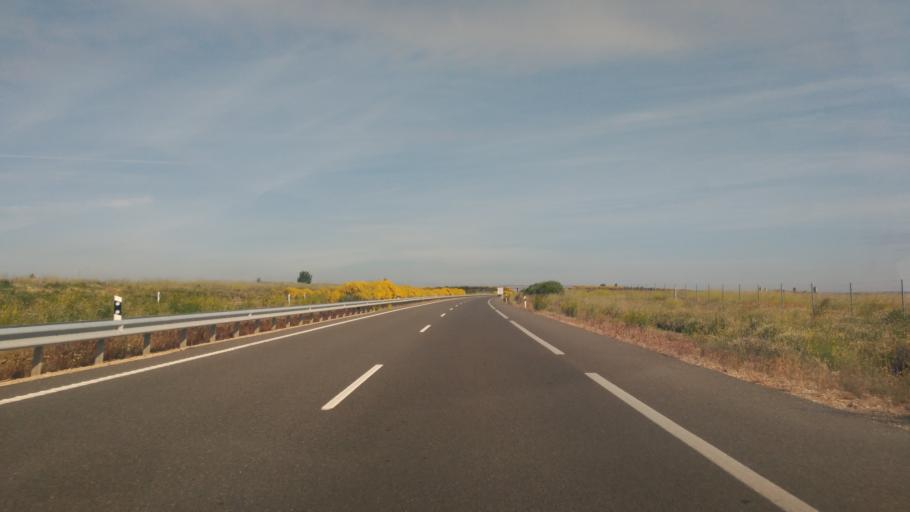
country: ES
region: Castille and Leon
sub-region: Provincia de Salamanca
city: Castellanos de Villiquera
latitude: 41.0563
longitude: -5.6770
